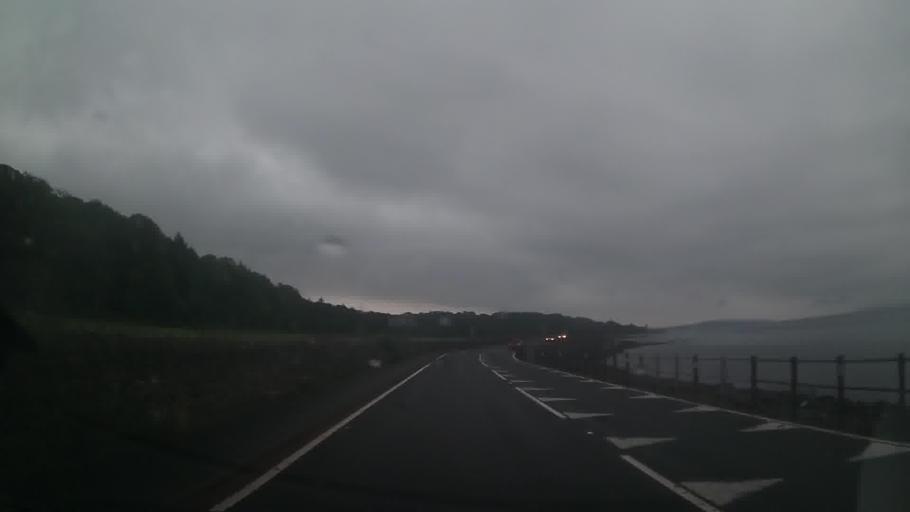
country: GB
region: Scotland
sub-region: North Ayrshire
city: Skelmorlie
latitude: 55.8548
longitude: -4.8893
